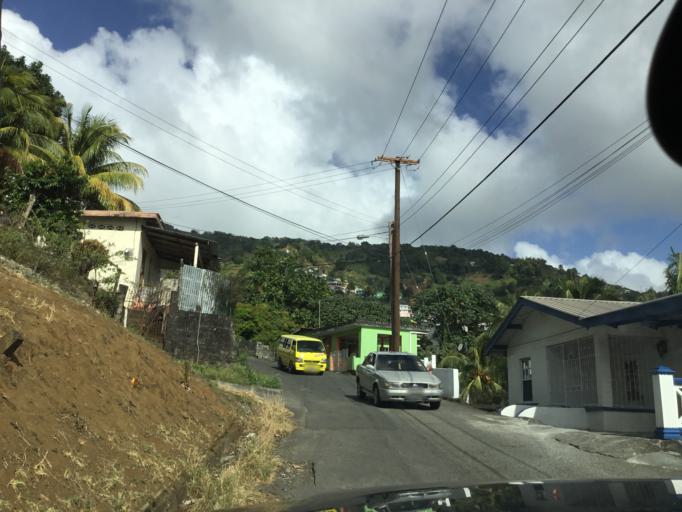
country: VC
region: Saint George
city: Kingstown
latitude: 13.1664
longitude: -61.2211
